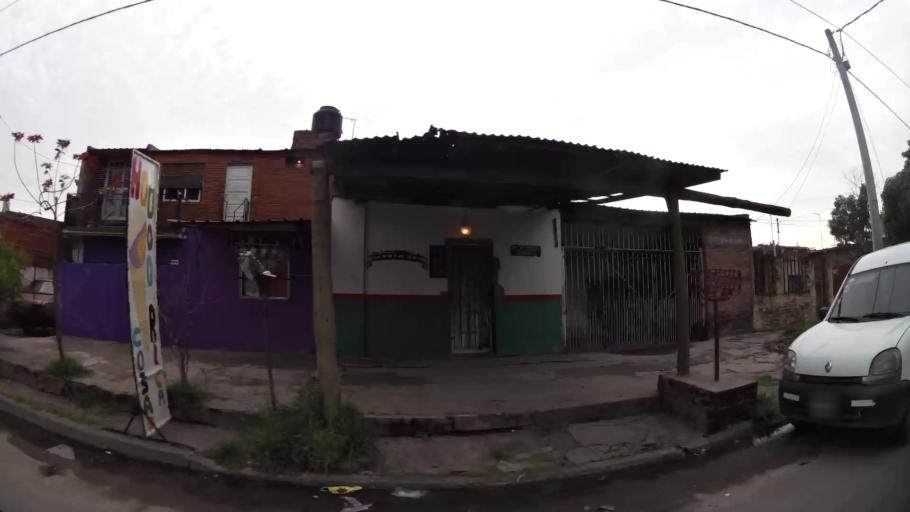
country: AR
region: Buenos Aires
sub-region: Partido de Lanus
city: Lanus
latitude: -34.7209
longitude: -58.3492
